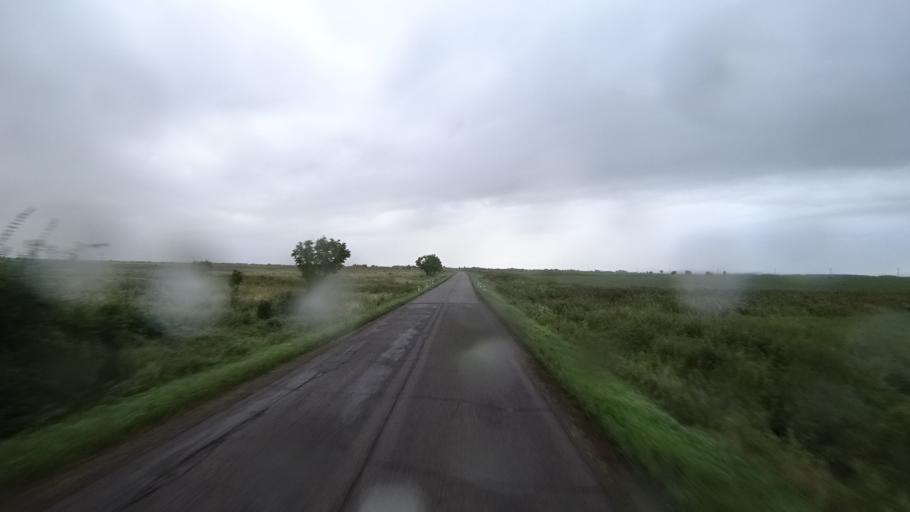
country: RU
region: Primorskiy
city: Chernigovka
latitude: 44.3855
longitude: 132.5295
